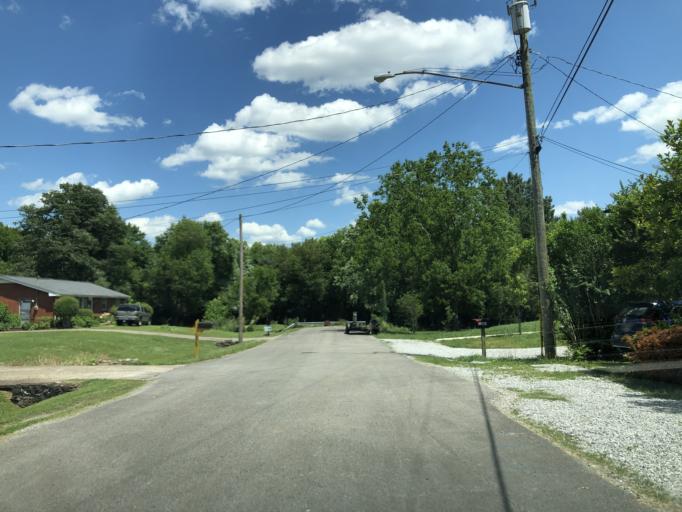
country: US
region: Tennessee
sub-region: Davidson County
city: Nashville
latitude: 36.1744
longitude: -86.7189
